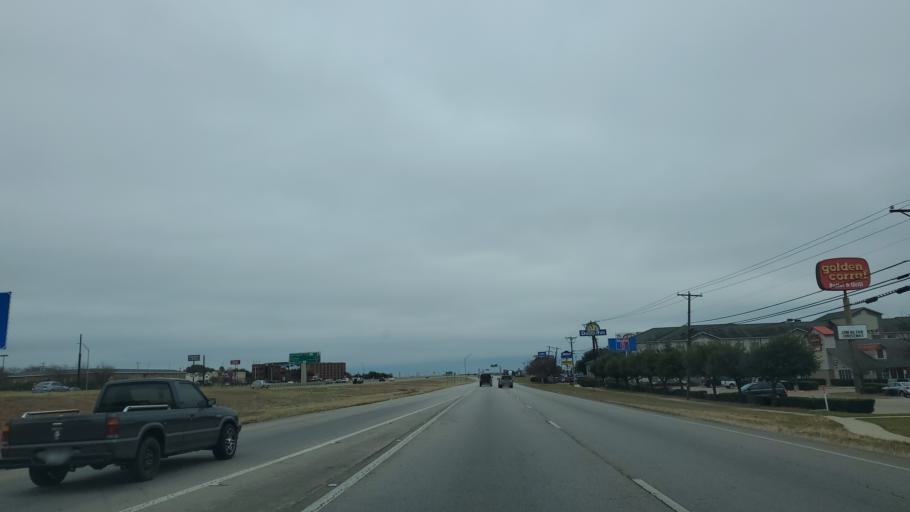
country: US
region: Texas
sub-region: Bell County
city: Killeen
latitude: 31.0932
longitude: -97.7288
